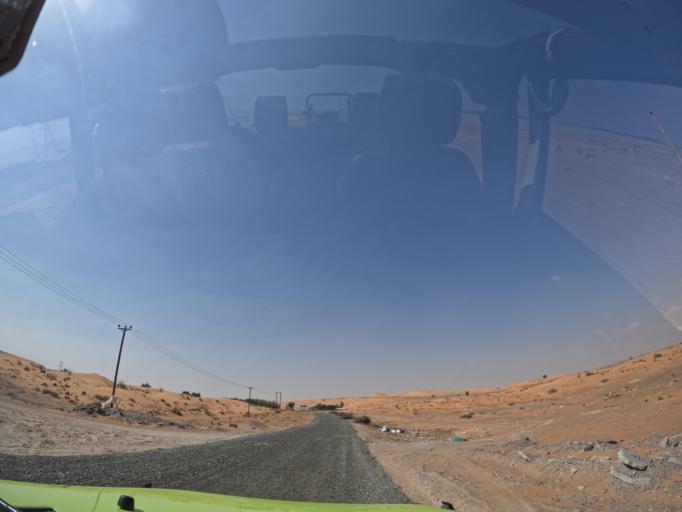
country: AE
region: Ash Shariqah
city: Adh Dhayd
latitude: 24.7955
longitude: 55.8020
